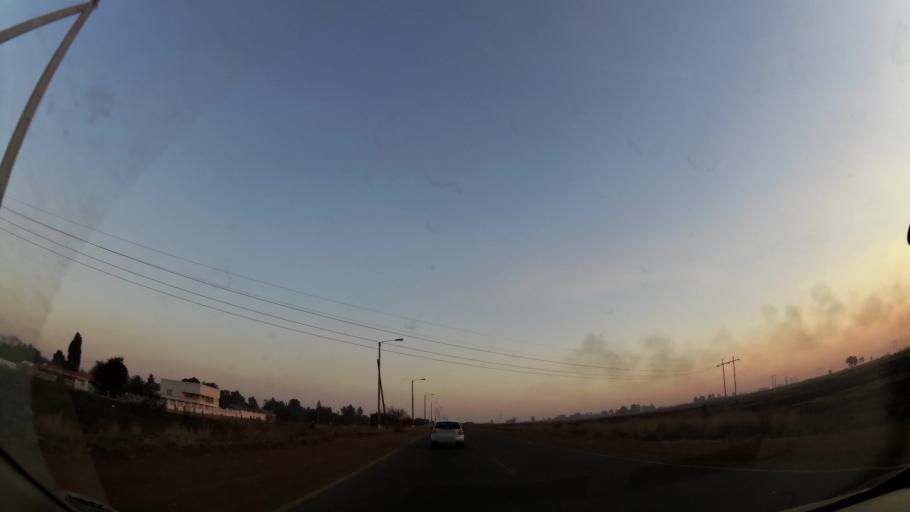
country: ZA
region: Gauteng
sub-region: Ekurhuleni Metropolitan Municipality
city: Springs
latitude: -26.3368
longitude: 28.4210
